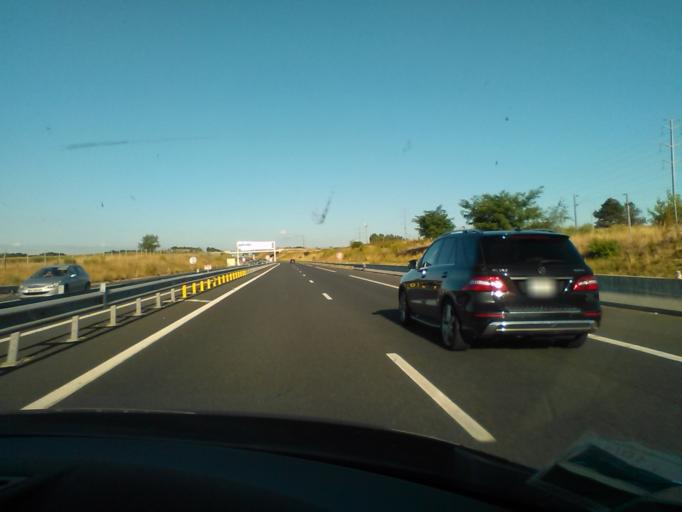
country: FR
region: Rhone-Alpes
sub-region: Departement de l'Ain
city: Mionnay
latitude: 45.8581
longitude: 4.9198
